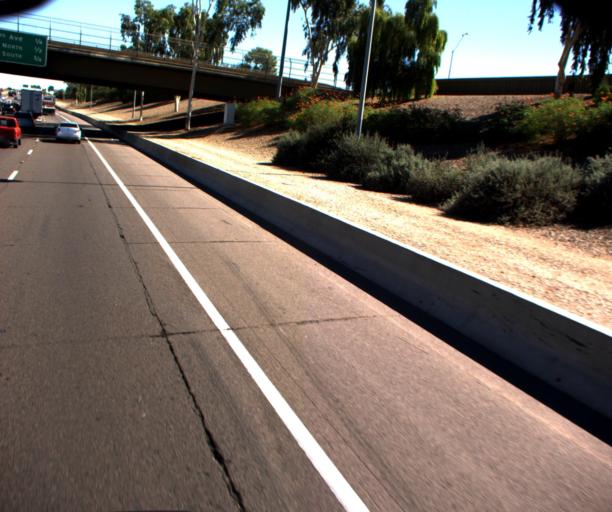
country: US
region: Arizona
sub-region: Maricopa County
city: Phoenix
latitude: 33.4618
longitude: -112.1266
